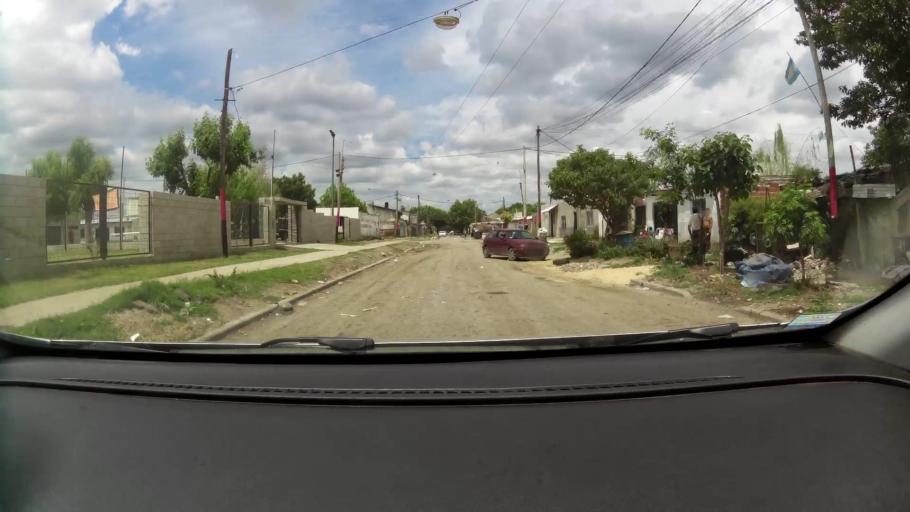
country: AR
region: Santa Fe
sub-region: Departamento de Rosario
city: Rosario
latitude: -32.9804
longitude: -60.6590
